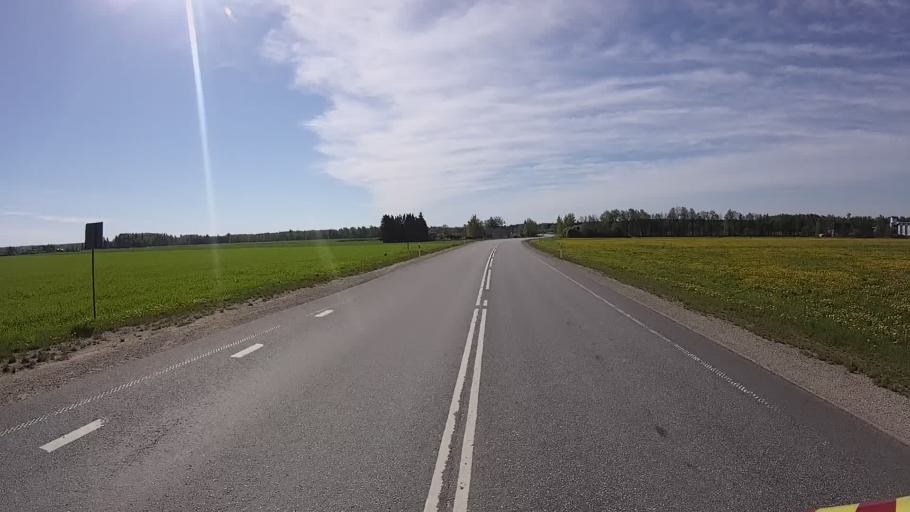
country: EE
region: Tartu
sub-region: Tartu linn
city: Tartu
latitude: 58.3667
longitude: 26.8853
